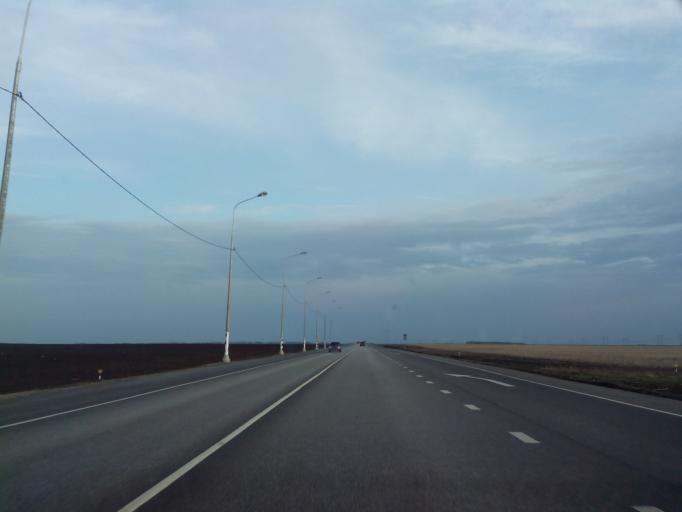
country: RU
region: Rjazan
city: Ryazhsk
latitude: 53.5766
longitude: 40.0443
